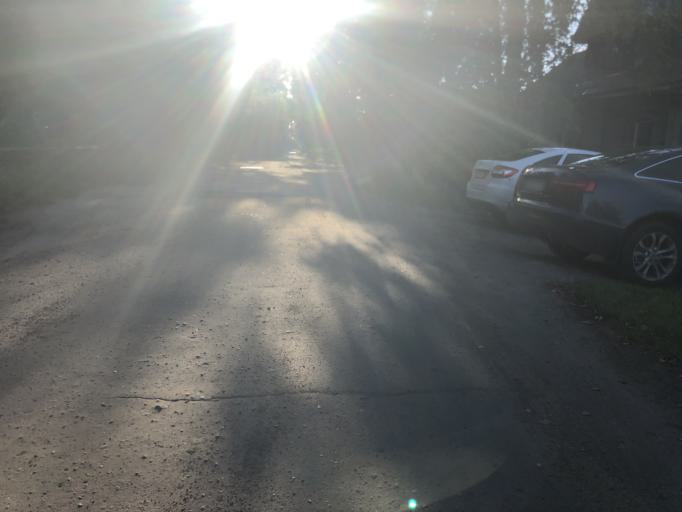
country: RU
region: Tverskaya
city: Rzhev
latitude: 56.2434
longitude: 34.3337
